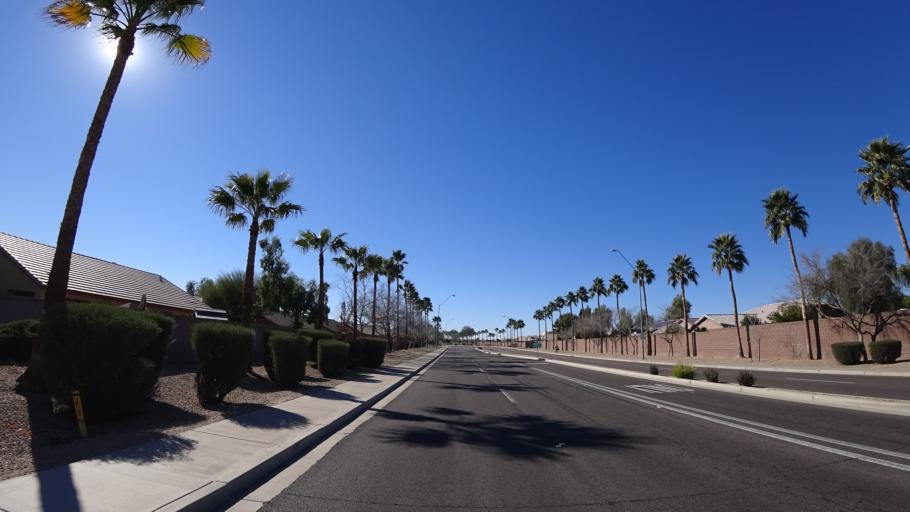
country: US
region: Arizona
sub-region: Maricopa County
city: Goodyear
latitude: 33.4258
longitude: -112.3928
